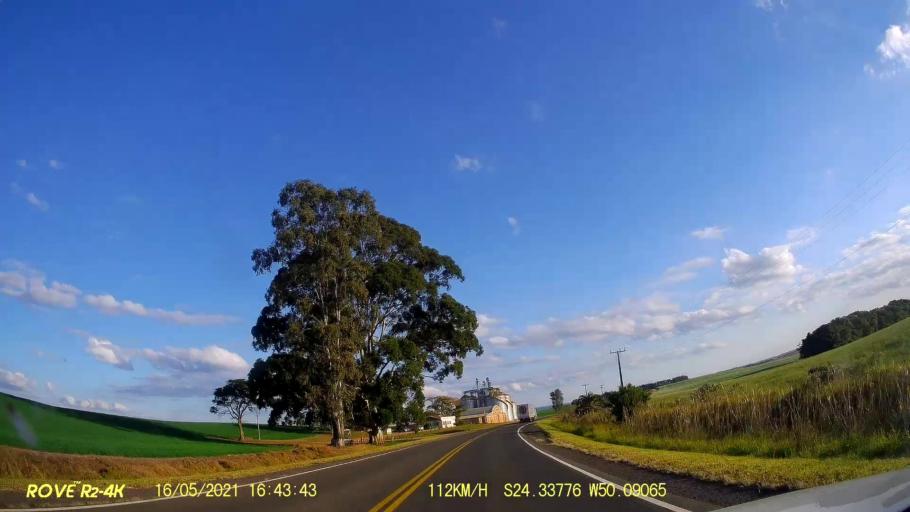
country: BR
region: Parana
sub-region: Pirai Do Sul
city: Pirai do Sul
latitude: -24.3379
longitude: -50.0908
